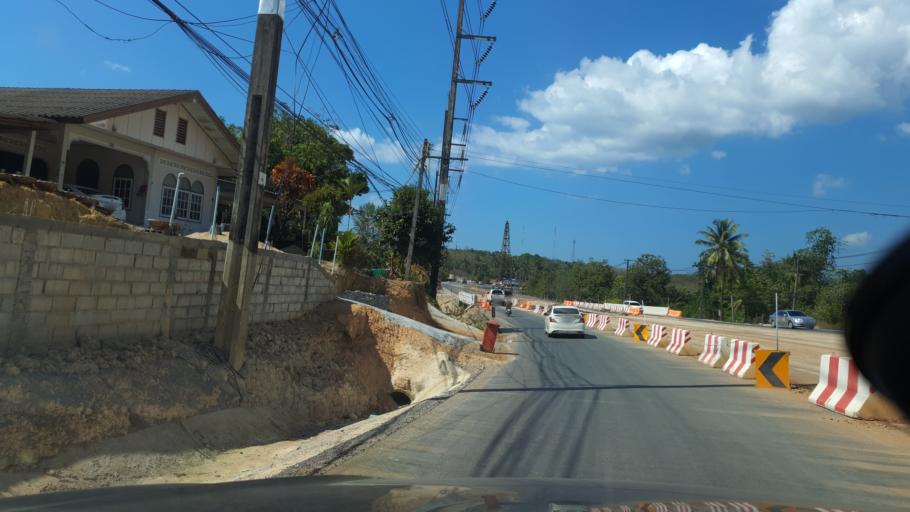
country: TH
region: Phangnga
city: Ban Khao Lak
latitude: 8.5600
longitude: 98.2695
